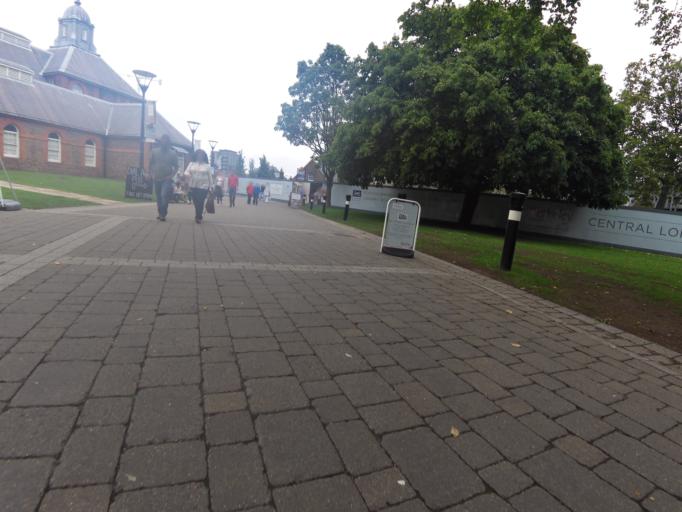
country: GB
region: England
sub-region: Greater London
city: Woolwich
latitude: 51.4920
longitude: 0.0696
